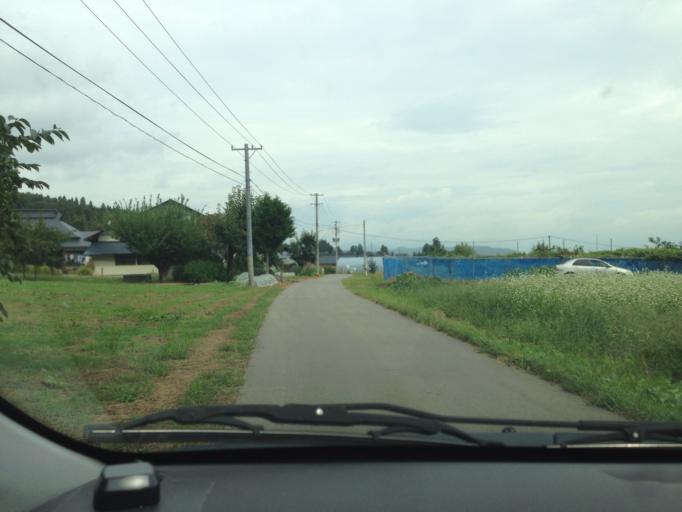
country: JP
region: Fukushima
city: Kitakata
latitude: 37.5585
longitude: 139.8004
